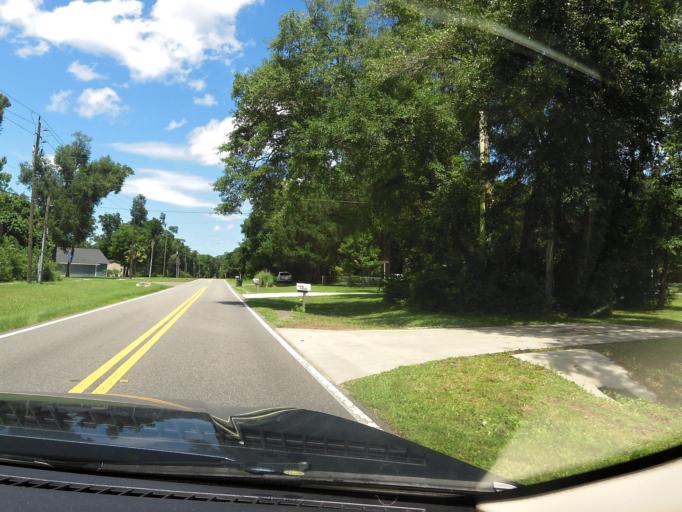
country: US
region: Florida
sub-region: Nassau County
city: Fernandina Beach
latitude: 30.6599
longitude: -81.5300
